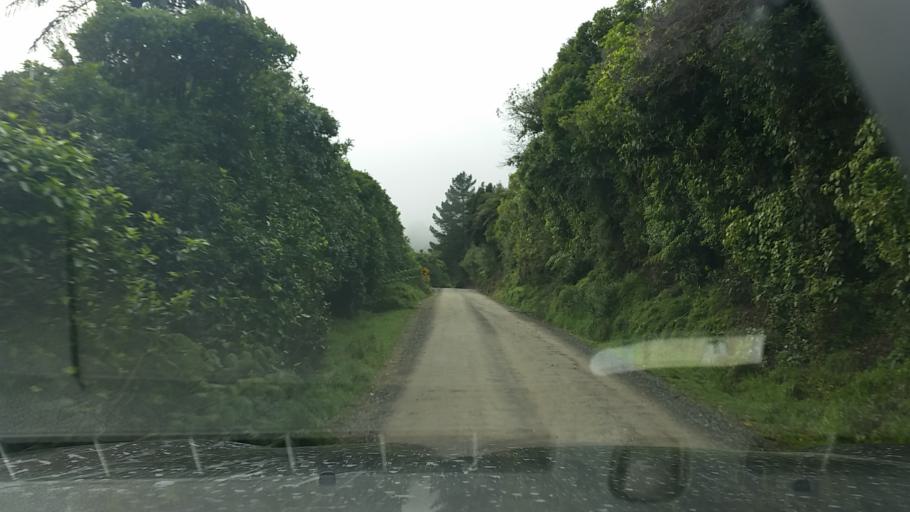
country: NZ
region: Marlborough
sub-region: Marlborough District
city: Picton
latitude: -41.1704
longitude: 174.0447
